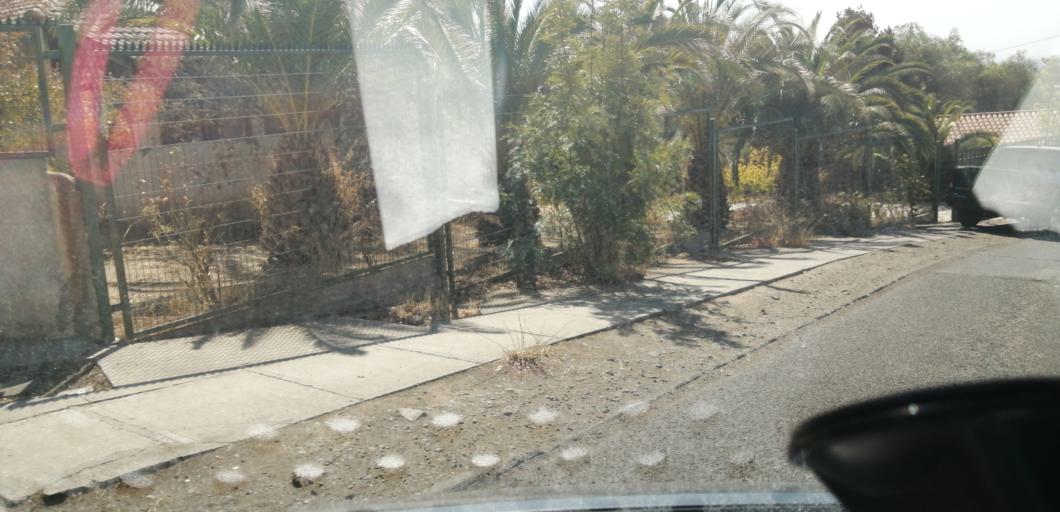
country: CL
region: Santiago Metropolitan
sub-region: Provincia de Santiago
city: Lo Prado
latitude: -33.4555
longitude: -70.8244
